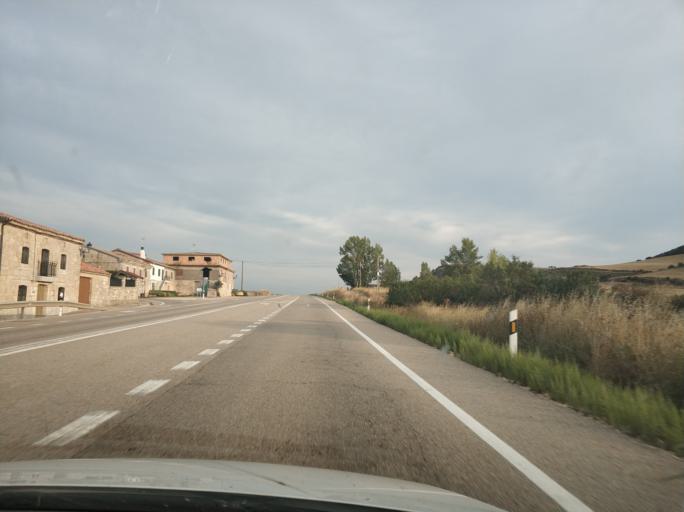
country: ES
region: Castille and Leon
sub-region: Provincia de Burgos
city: Cubillo del Campo
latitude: 42.1676
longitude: -3.6126
